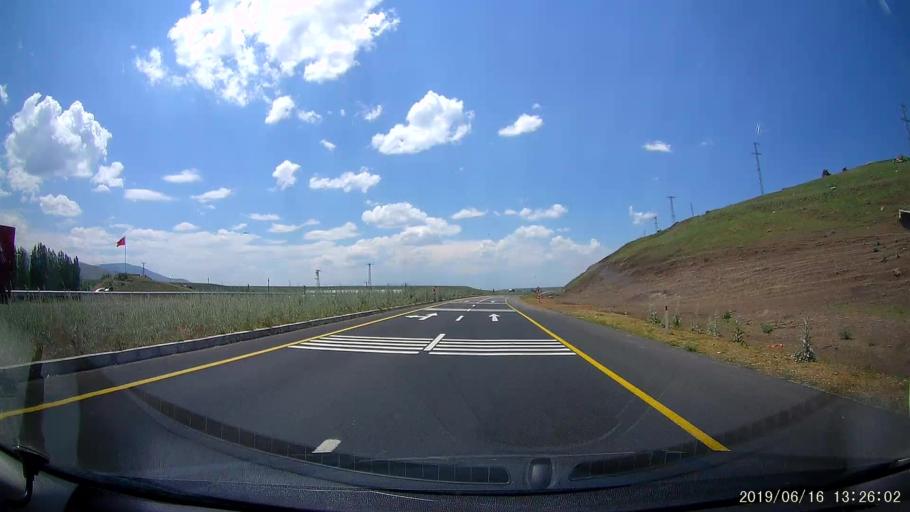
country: TR
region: Agri
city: Taslicay
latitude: 39.6569
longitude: 43.3380
